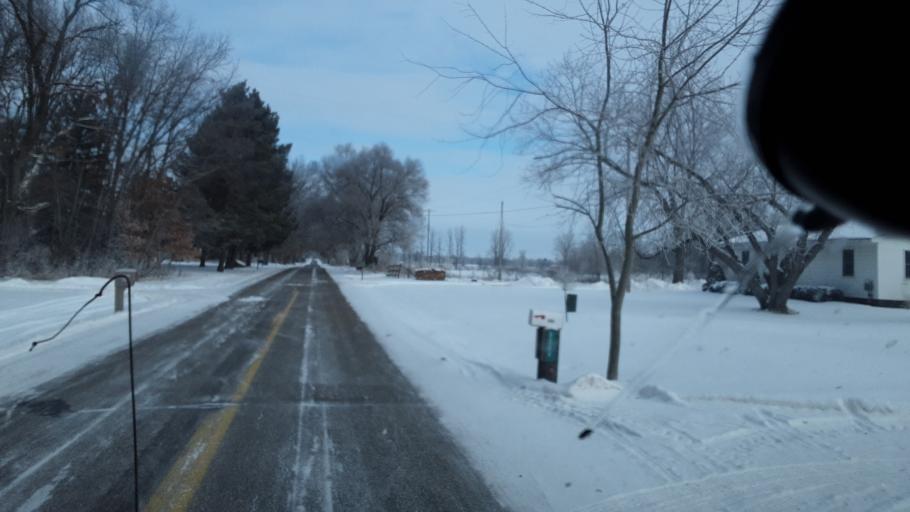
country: US
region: Michigan
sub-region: Ingham County
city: Leslie
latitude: 42.3781
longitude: -84.4924
